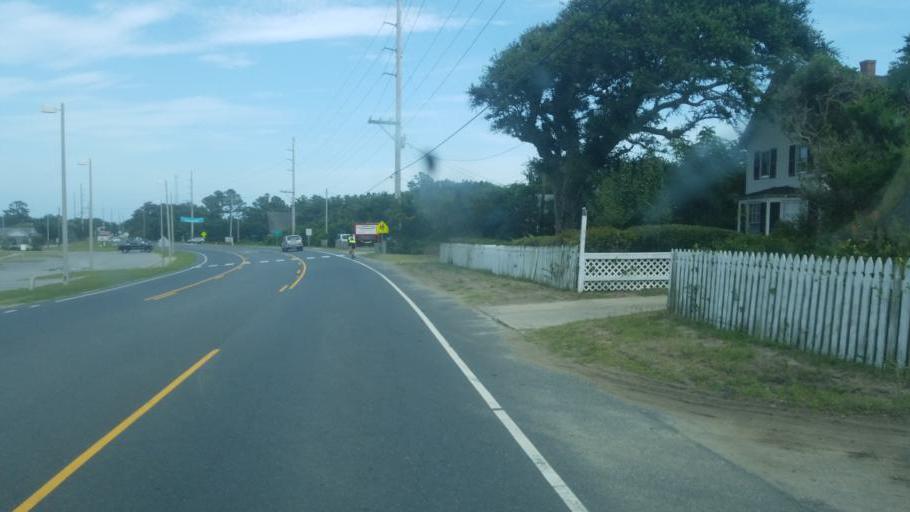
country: US
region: North Carolina
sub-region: Dare County
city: Buxton
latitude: 35.2645
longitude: -75.5524
